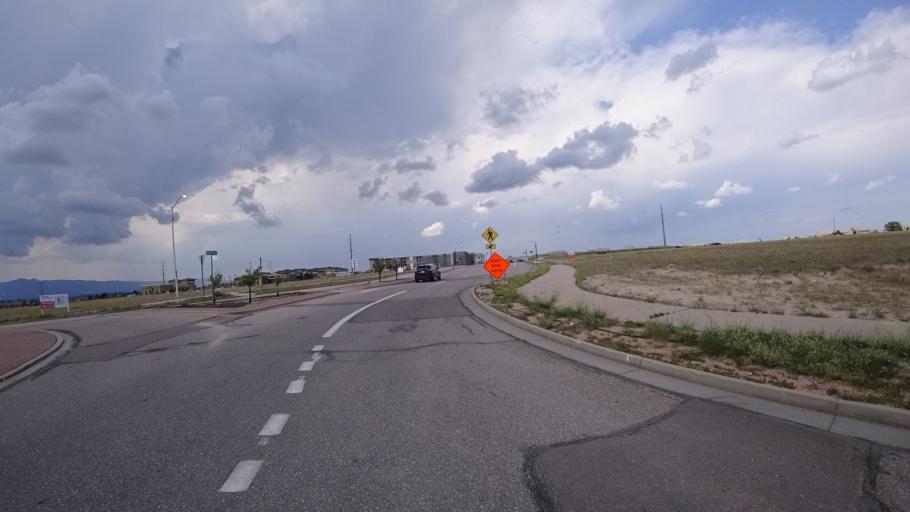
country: US
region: Colorado
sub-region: El Paso County
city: Black Forest
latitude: 38.9386
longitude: -104.7109
